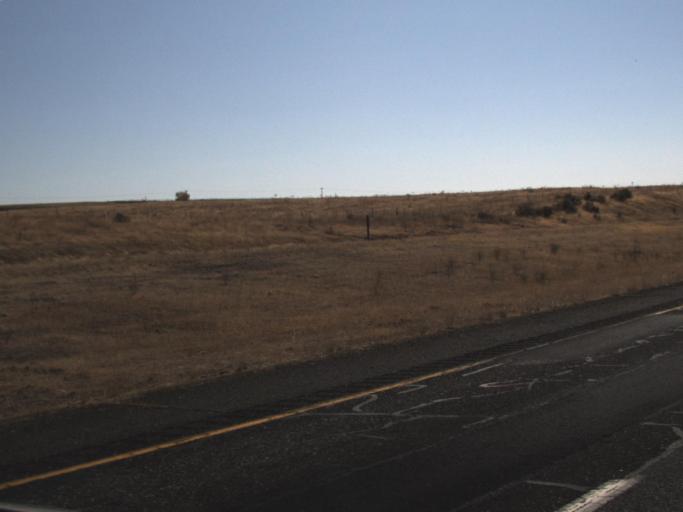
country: US
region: Washington
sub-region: Franklin County
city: Basin City
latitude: 46.5288
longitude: -119.0152
